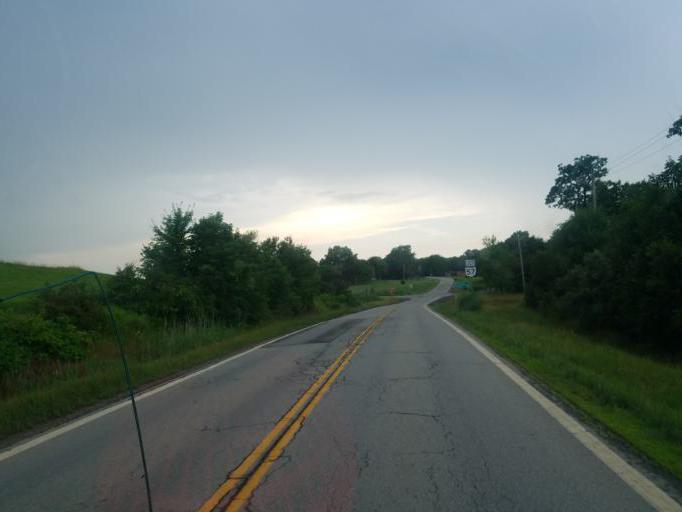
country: US
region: Ohio
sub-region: Wayne County
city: Rittman
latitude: 40.9458
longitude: -81.7615
